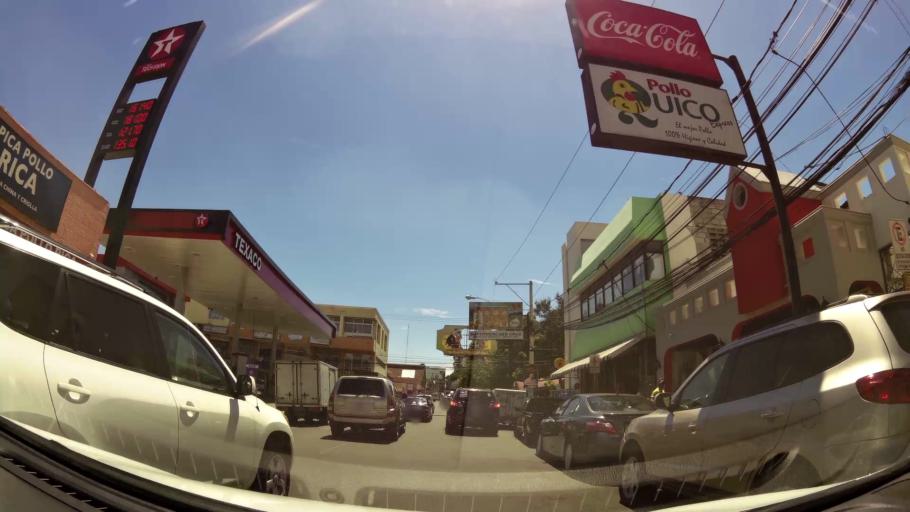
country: DO
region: Santiago
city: Santiago de los Caballeros
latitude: 19.4529
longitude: -70.6977
